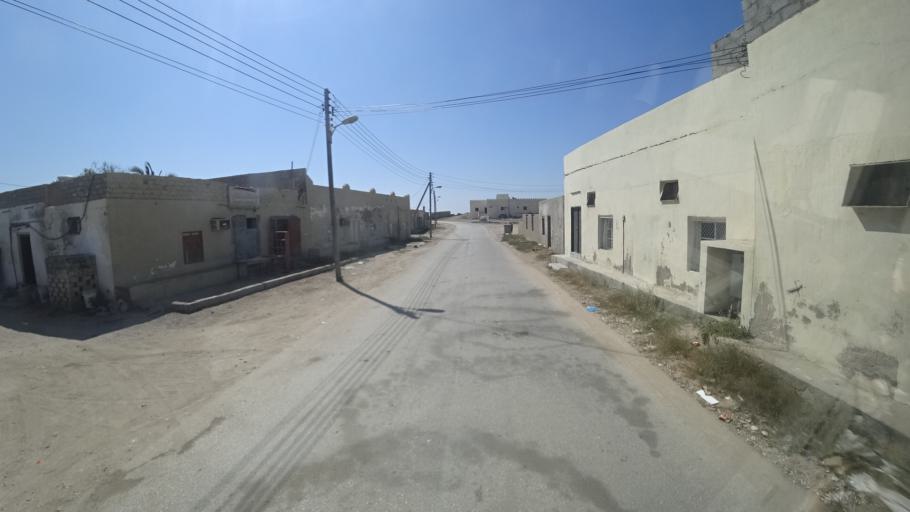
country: OM
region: Zufar
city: Salalah
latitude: 16.9643
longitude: 54.7452
